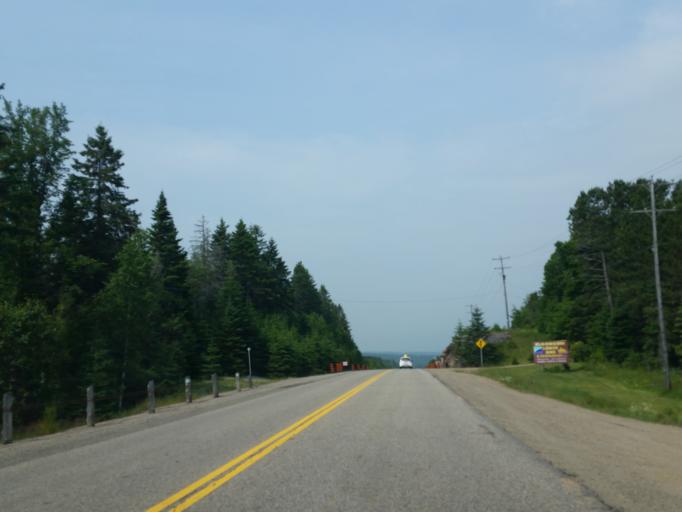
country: CA
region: Ontario
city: Bancroft
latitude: 45.4958
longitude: -78.1909
